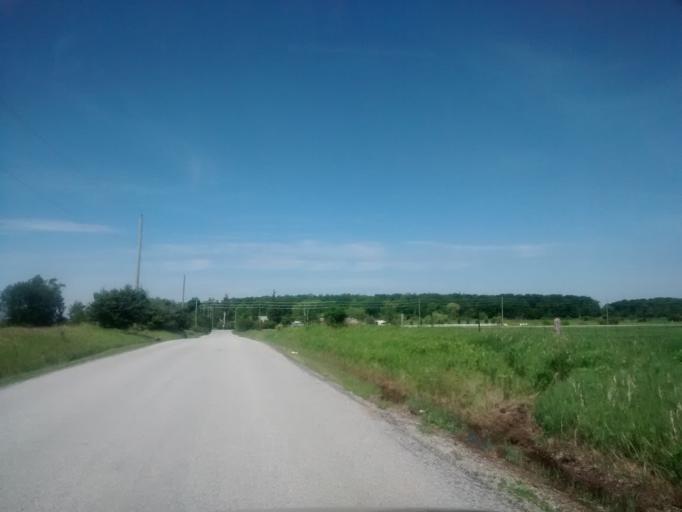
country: CA
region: Ontario
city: Burlington
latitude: 43.4388
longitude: -79.8225
